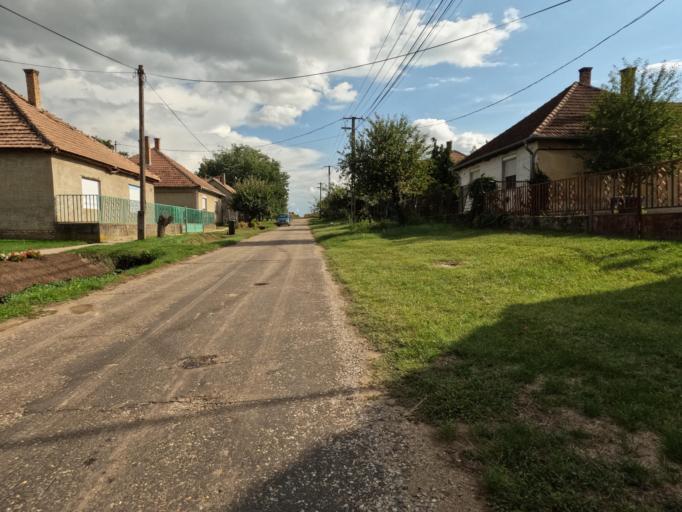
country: HU
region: Tolna
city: Tengelic
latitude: 46.5255
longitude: 18.7167
